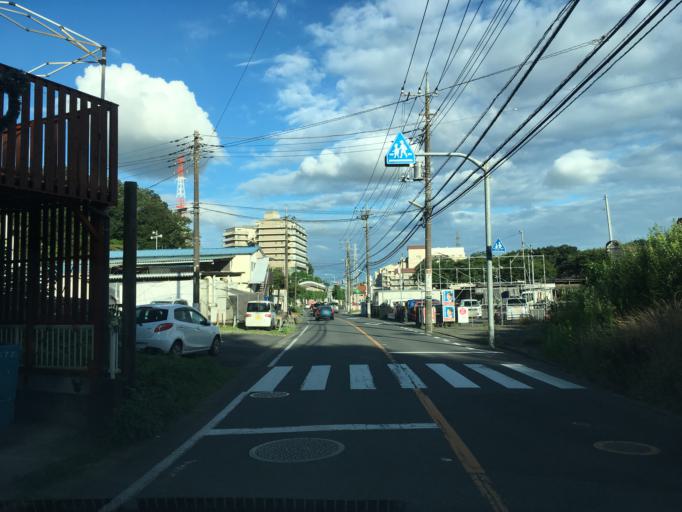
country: JP
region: Tokyo
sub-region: Machida-shi
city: Machida
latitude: 35.5966
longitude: 139.4430
